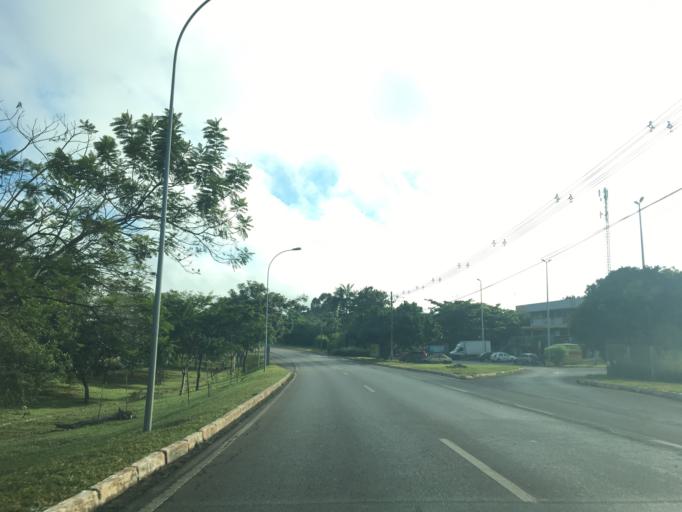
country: BR
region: Federal District
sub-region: Brasilia
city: Brasilia
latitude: -15.8236
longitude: -47.8053
